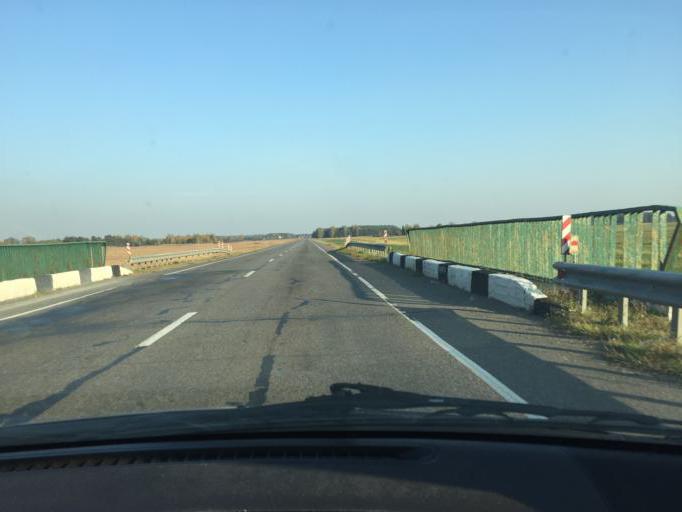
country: BY
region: Brest
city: Davyd-Haradok
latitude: 52.2432
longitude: 27.1685
